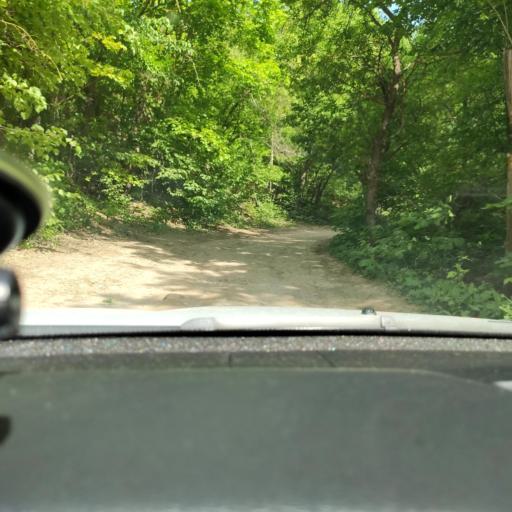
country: RU
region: Samara
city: Volzhskiy
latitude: 53.3386
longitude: 50.2137
